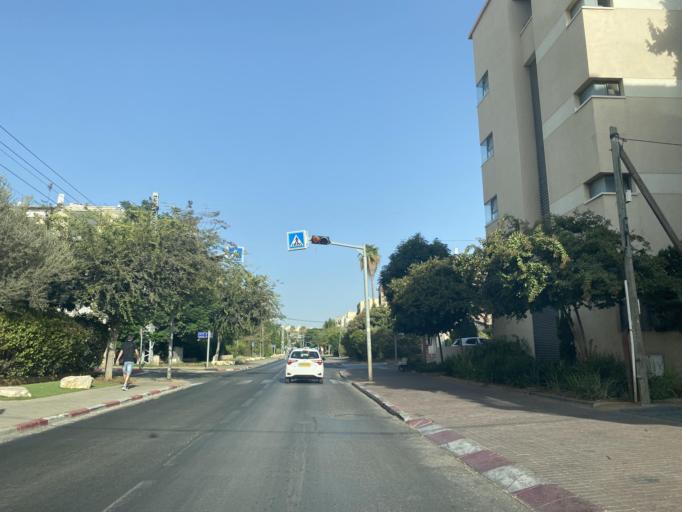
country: IL
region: Tel Aviv
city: Ramat HaSharon
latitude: 32.1648
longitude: 34.8456
